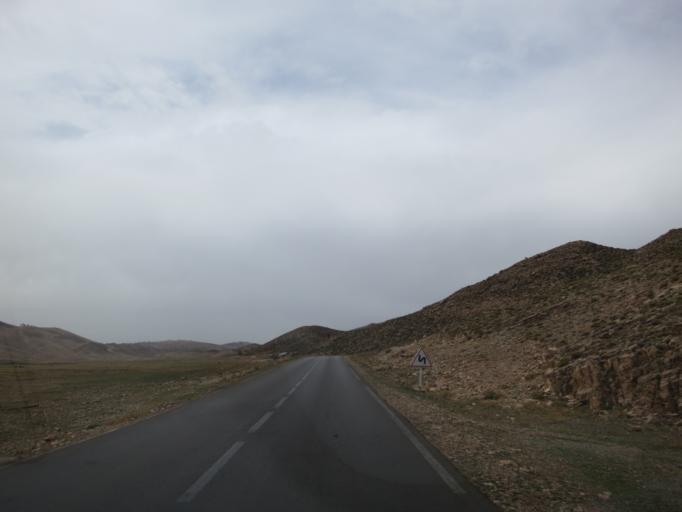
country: MA
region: Meknes-Tafilalet
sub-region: Khenifra
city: Itzer
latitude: 33.0691
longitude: -5.0275
